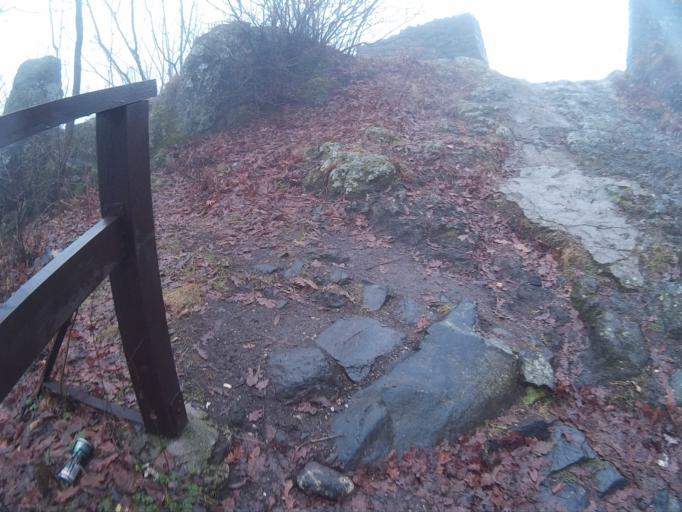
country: HU
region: Nograd
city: Somoskoujfalu
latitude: 48.1445
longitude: 19.8467
